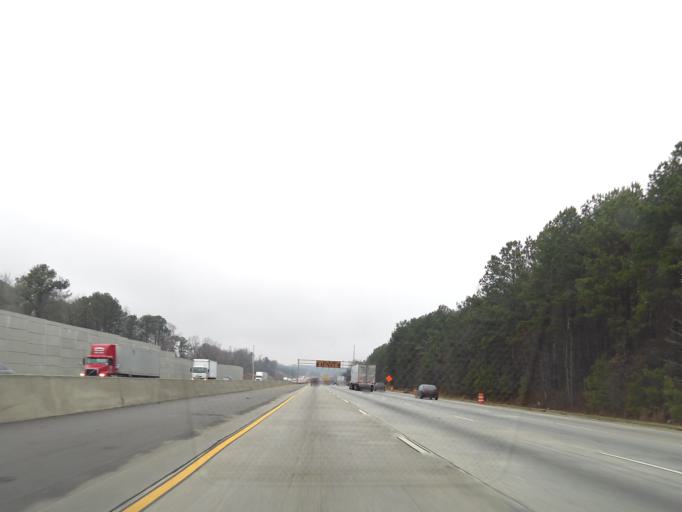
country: US
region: Georgia
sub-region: Henry County
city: Stockbridge
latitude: 33.5278
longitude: -84.2550
